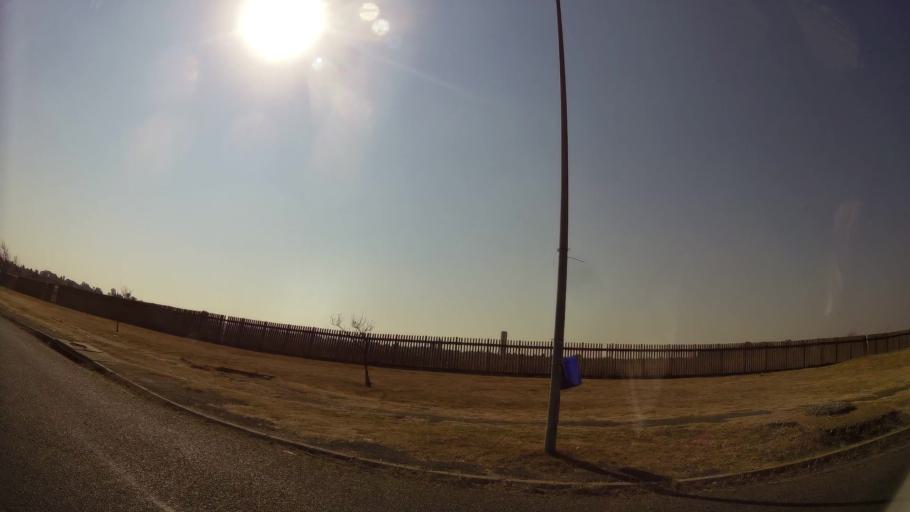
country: ZA
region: Gauteng
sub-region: Ekurhuleni Metropolitan Municipality
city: Boksburg
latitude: -26.2383
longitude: 28.2609
